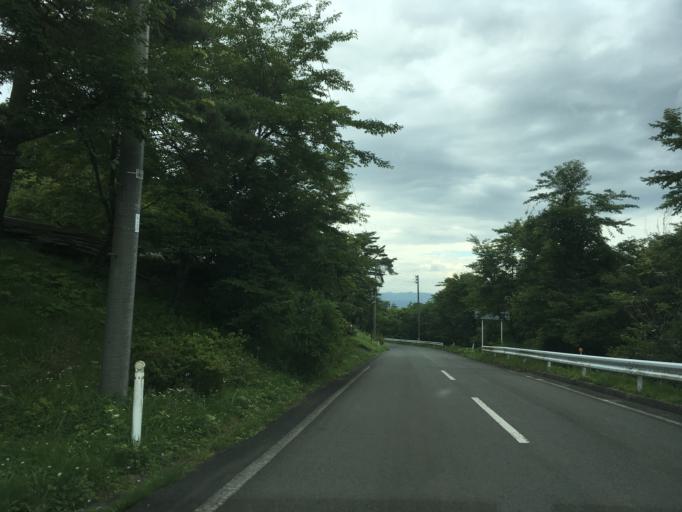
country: JP
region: Iwate
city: Ichinoseki
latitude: 38.8687
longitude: 141.3989
